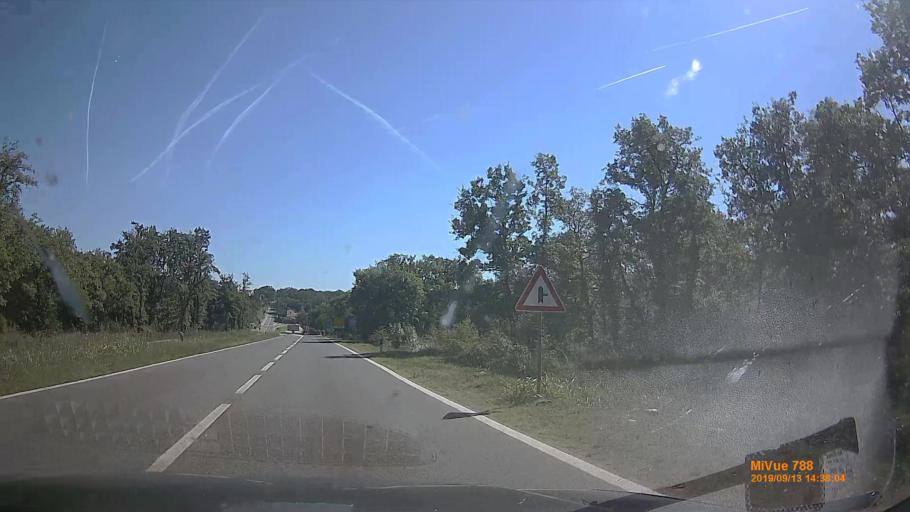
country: HR
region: Istarska
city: Umag
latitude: 45.4046
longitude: 13.5354
